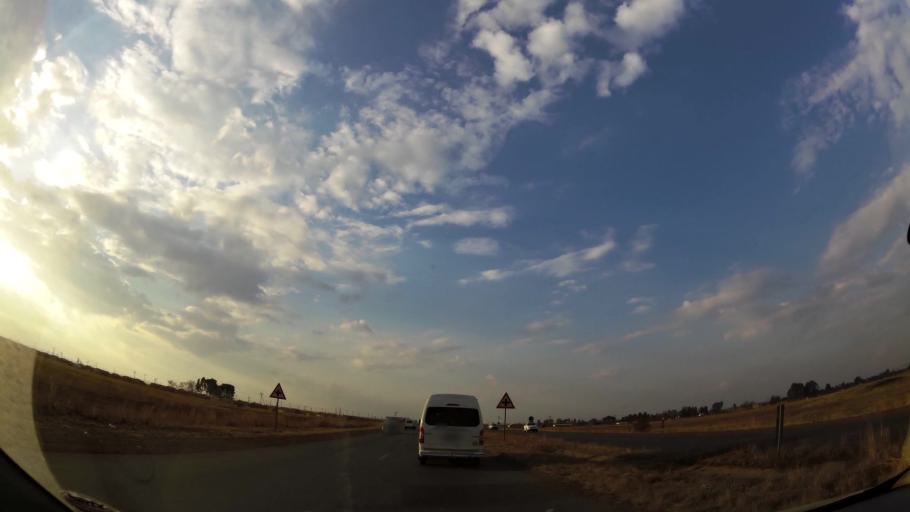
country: ZA
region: Gauteng
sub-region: Sedibeng District Municipality
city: Vanderbijlpark
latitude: -26.6225
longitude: 27.8116
